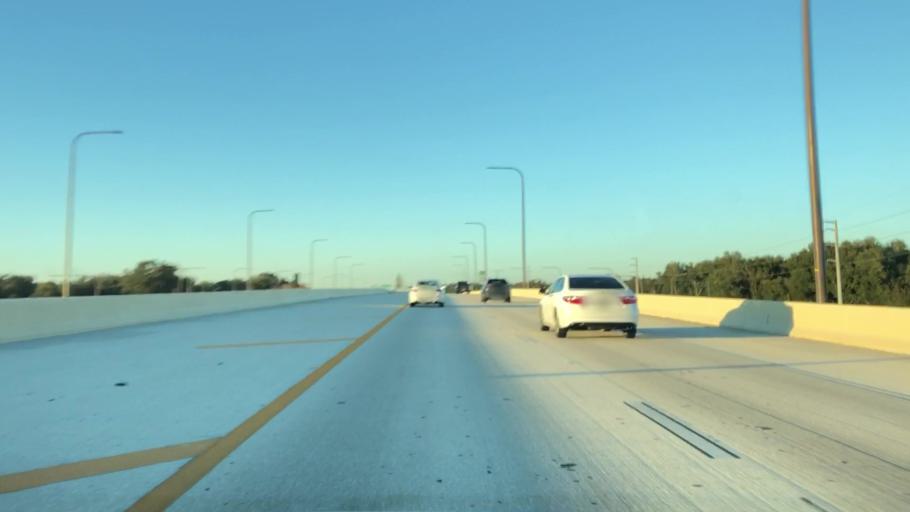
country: US
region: Florida
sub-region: Orange County
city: Apopka
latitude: 28.6978
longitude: -81.5591
